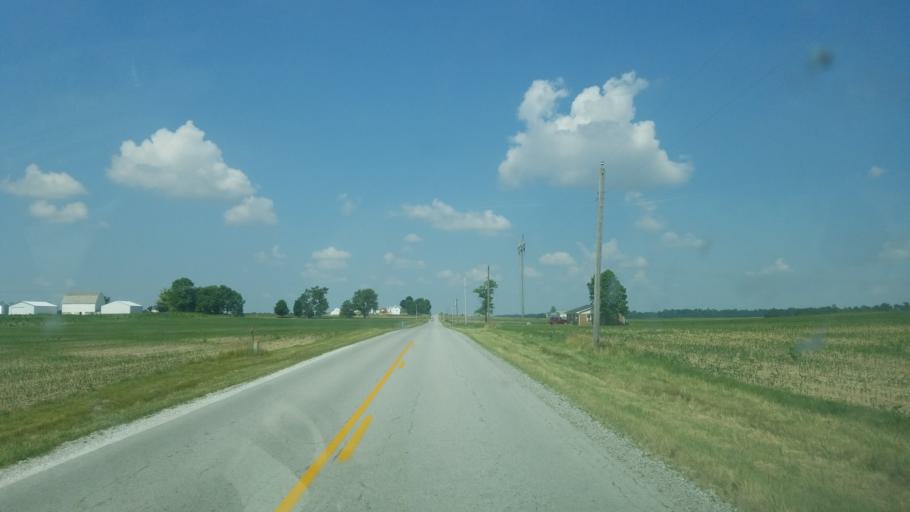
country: US
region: Ohio
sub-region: Auglaize County
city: Wapakoneta
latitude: 40.5706
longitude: -84.1146
